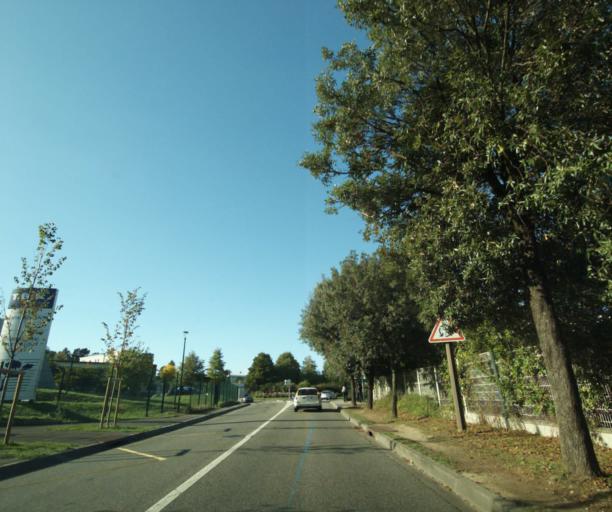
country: FR
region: Midi-Pyrenees
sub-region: Departement de la Haute-Garonne
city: Balma
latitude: 43.5835
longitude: 1.4932
